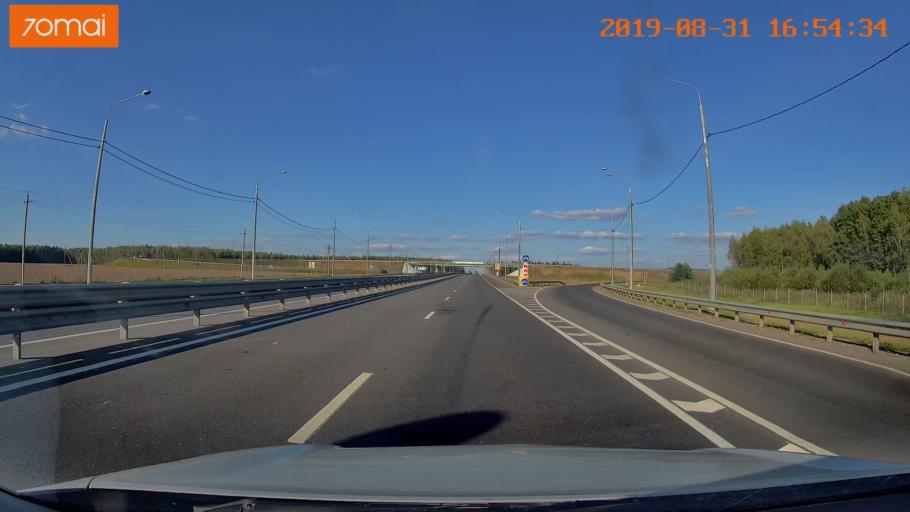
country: RU
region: Kaluga
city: Detchino
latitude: 54.7721
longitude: 36.2352
